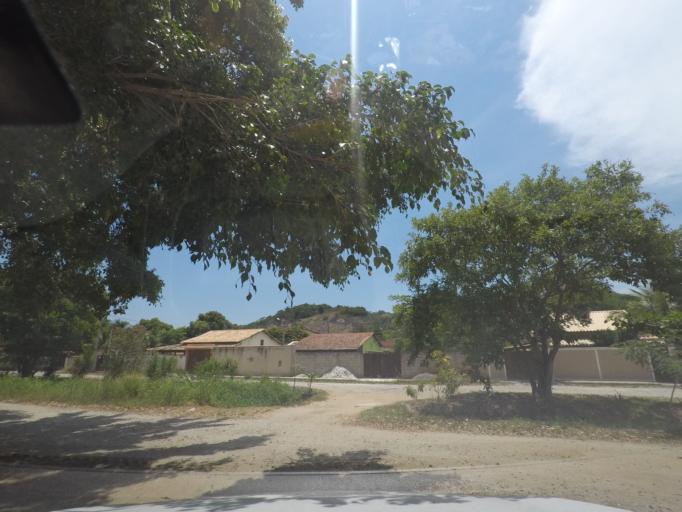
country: BR
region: Rio de Janeiro
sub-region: Marica
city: Marica
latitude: -22.9545
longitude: -42.9659
